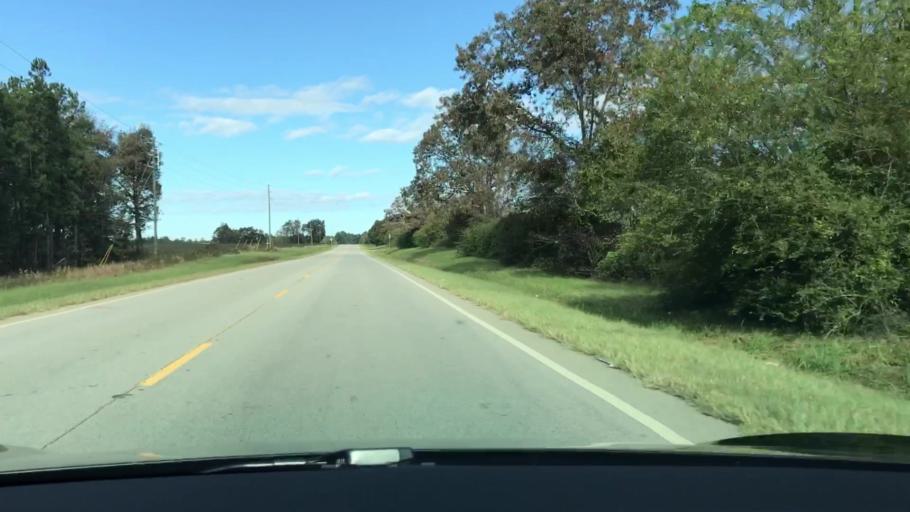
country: US
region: Georgia
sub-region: Jefferson County
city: Wrens
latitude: 33.1950
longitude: -82.4612
